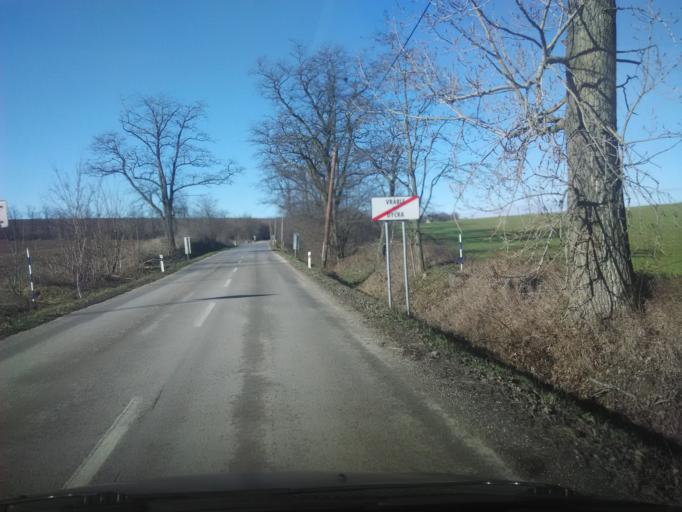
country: SK
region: Nitriansky
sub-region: Okres Nitra
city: Vrable
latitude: 48.2351
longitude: 18.2867
